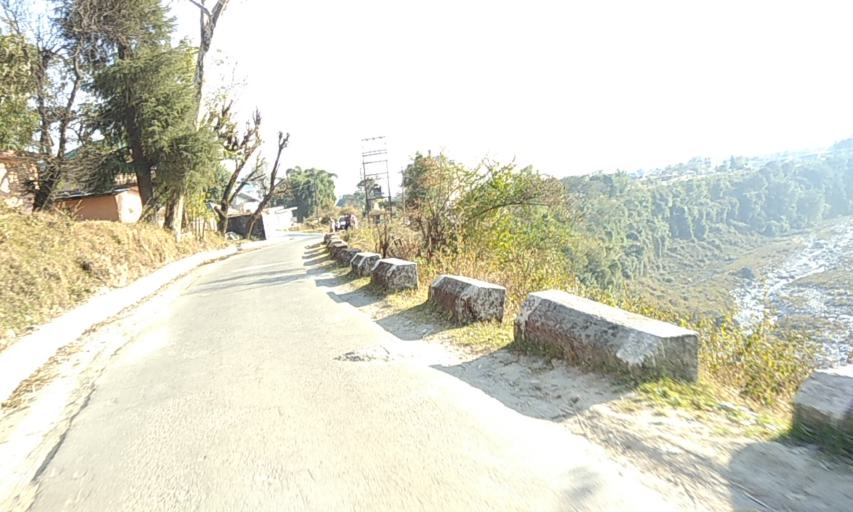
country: IN
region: Himachal Pradesh
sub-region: Kangra
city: Palampur
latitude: 32.1333
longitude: 76.5357
